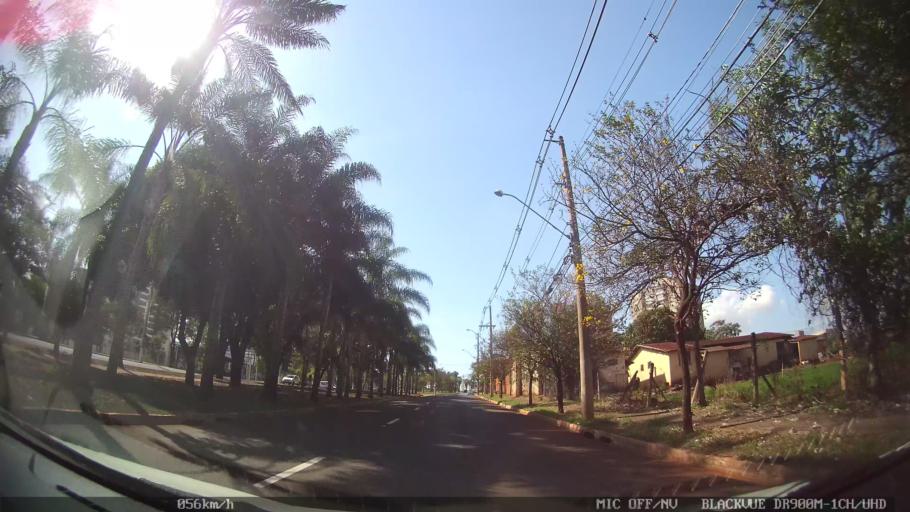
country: BR
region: Sao Paulo
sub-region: Ribeirao Preto
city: Ribeirao Preto
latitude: -21.2229
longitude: -47.8305
